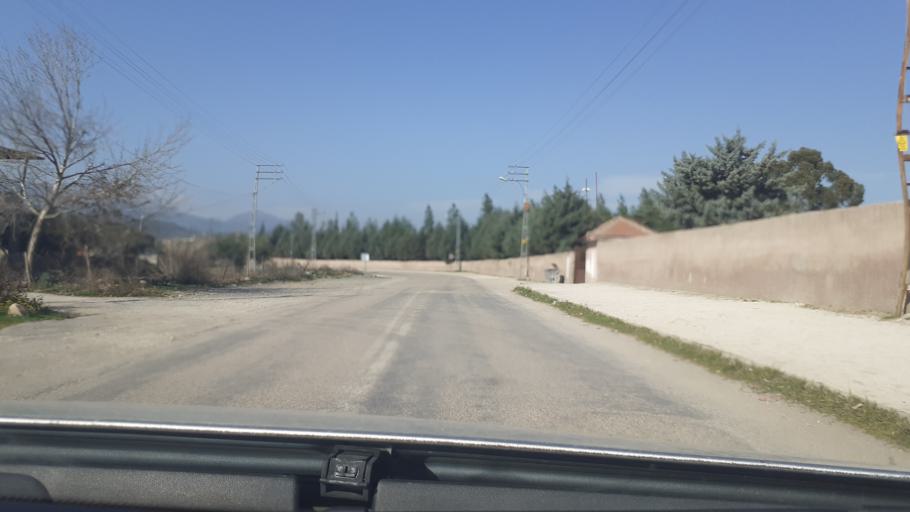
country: TR
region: Hatay
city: Aktepe
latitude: 36.7075
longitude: 36.4872
